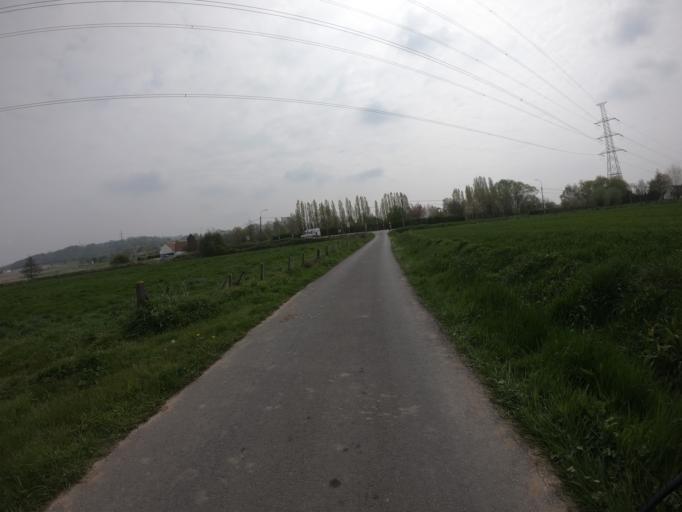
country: BE
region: Flanders
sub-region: Provincie West-Vlaanderen
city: Avelgem
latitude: 50.7576
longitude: 3.4630
